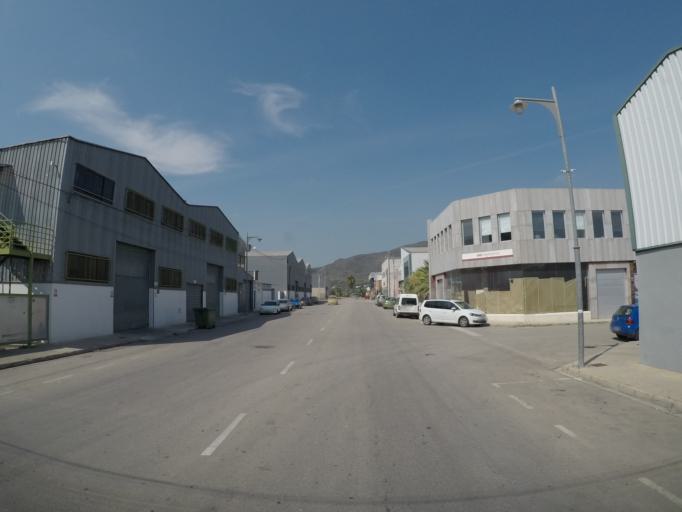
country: ES
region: Valencia
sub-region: Provincia de Alicante
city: Pego
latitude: 38.8469
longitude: -0.1126
